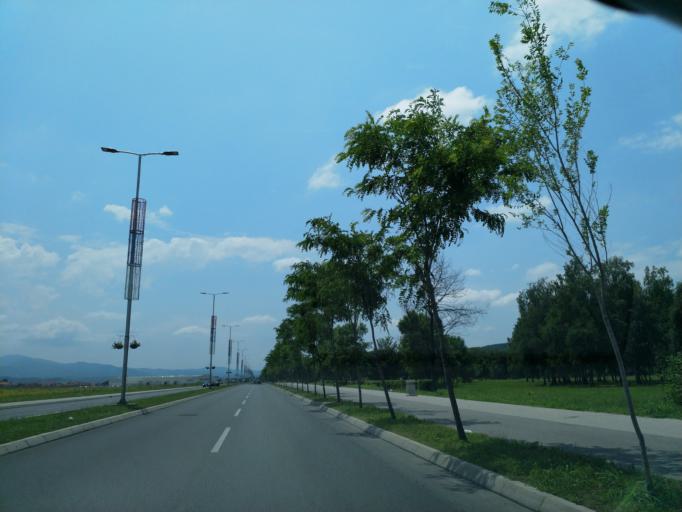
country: RS
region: Central Serbia
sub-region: Rasinski Okrug
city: Krusevac
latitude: 43.5663
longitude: 21.3360
